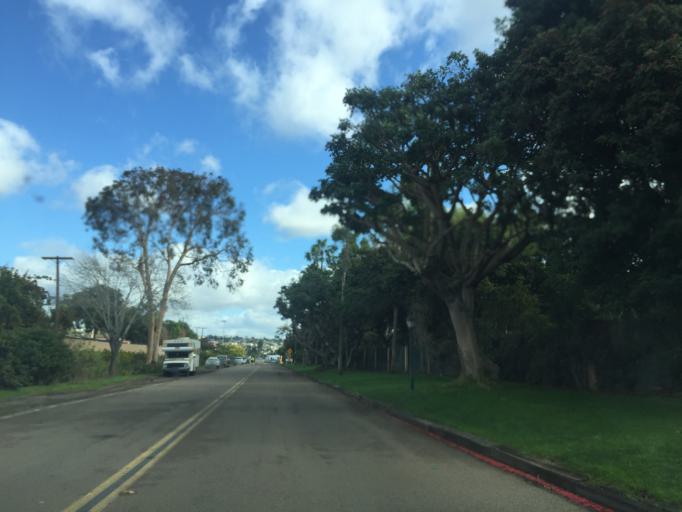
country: US
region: California
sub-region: San Diego County
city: La Jolla
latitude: 32.7966
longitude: -117.2279
